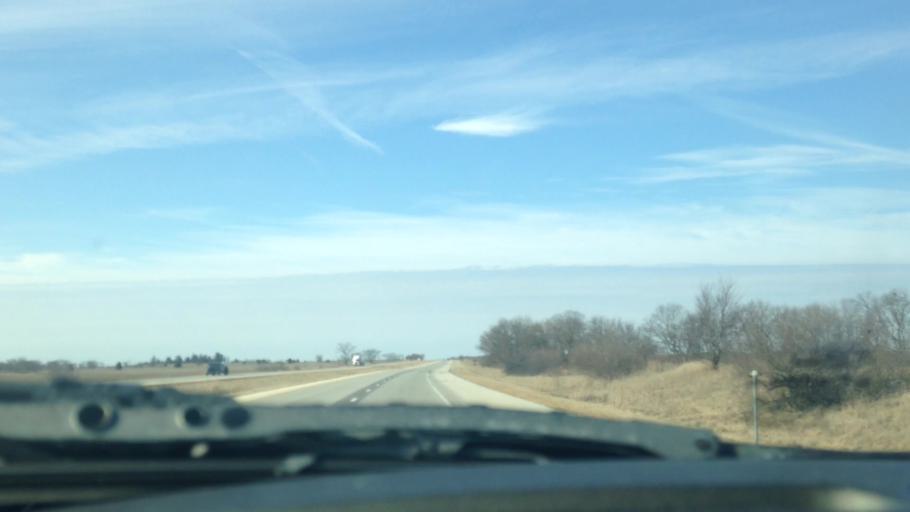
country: US
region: Illinois
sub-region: Ford County
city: Paxton
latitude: 40.5413
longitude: -88.0677
